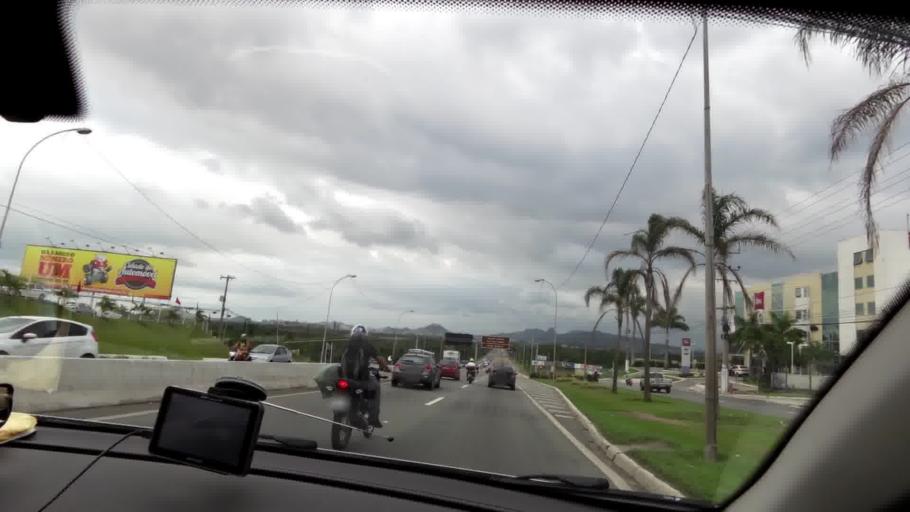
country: BR
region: Espirito Santo
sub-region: Vila Velha
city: Vila Velha
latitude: -20.2381
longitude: -40.2783
